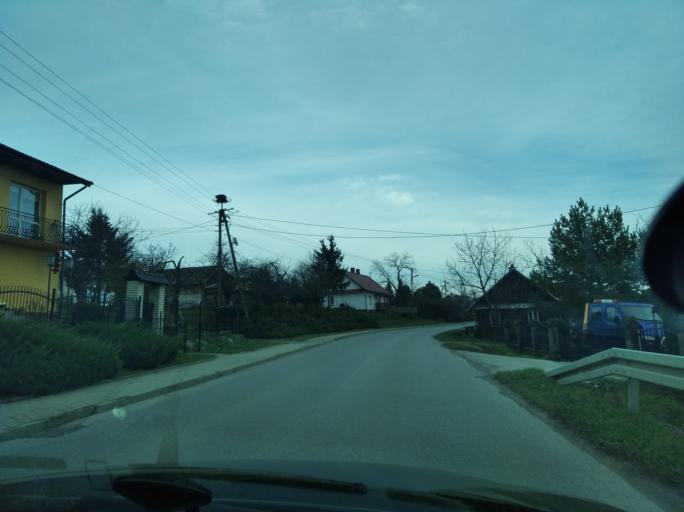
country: PL
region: Subcarpathian Voivodeship
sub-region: Powiat przeworski
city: Debow
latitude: 50.0483
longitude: 22.4626
